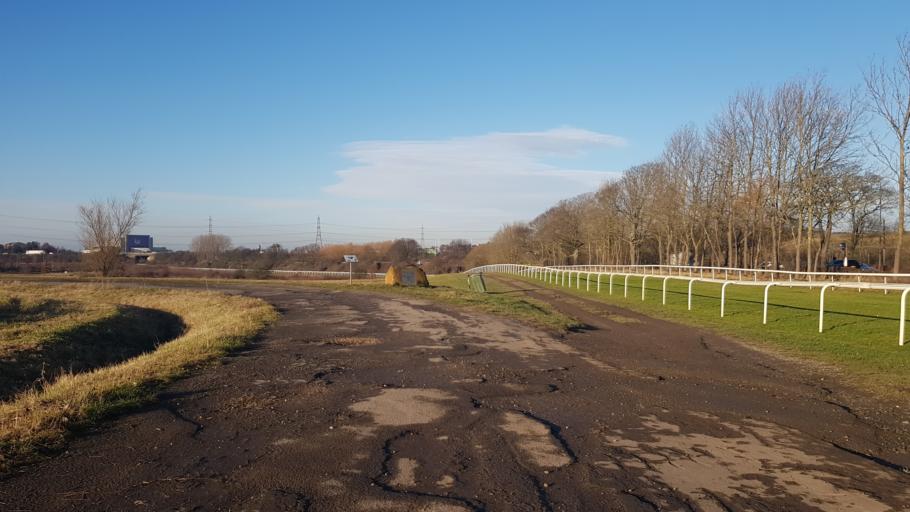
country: GB
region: England
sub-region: City and Borough of Wakefield
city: Pontefract
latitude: 53.7021
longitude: -1.3274
